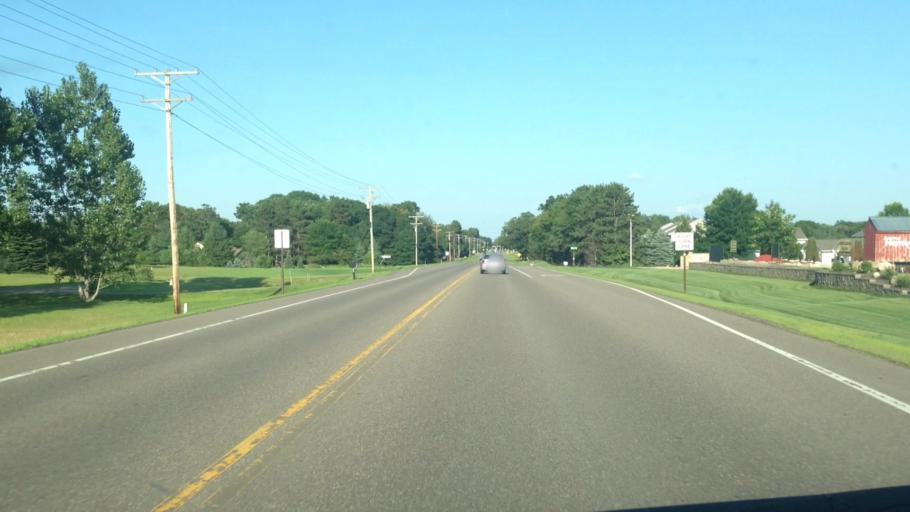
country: US
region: Minnesota
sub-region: Sherburne County
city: Zimmerman
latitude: 45.4436
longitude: -93.6089
